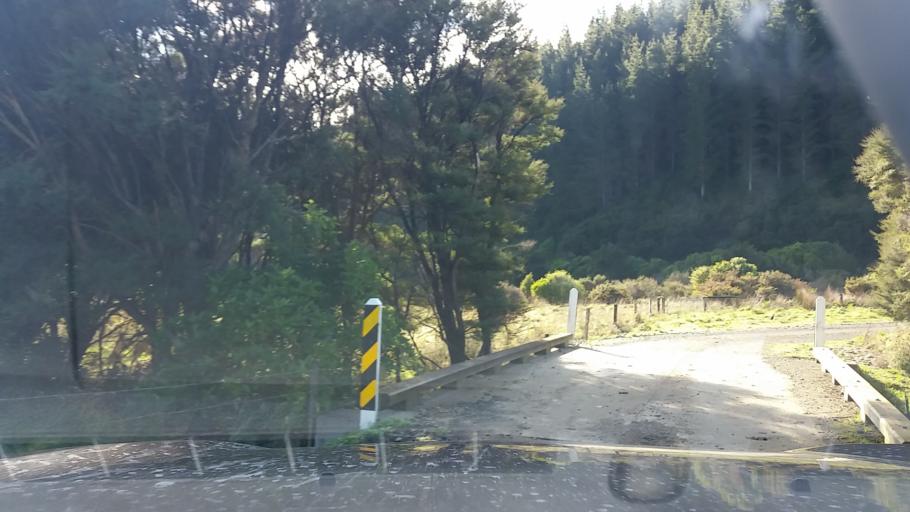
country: NZ
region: Marlborough
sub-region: Marlborough District
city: Picton
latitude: -41.1512
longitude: 173.9680
